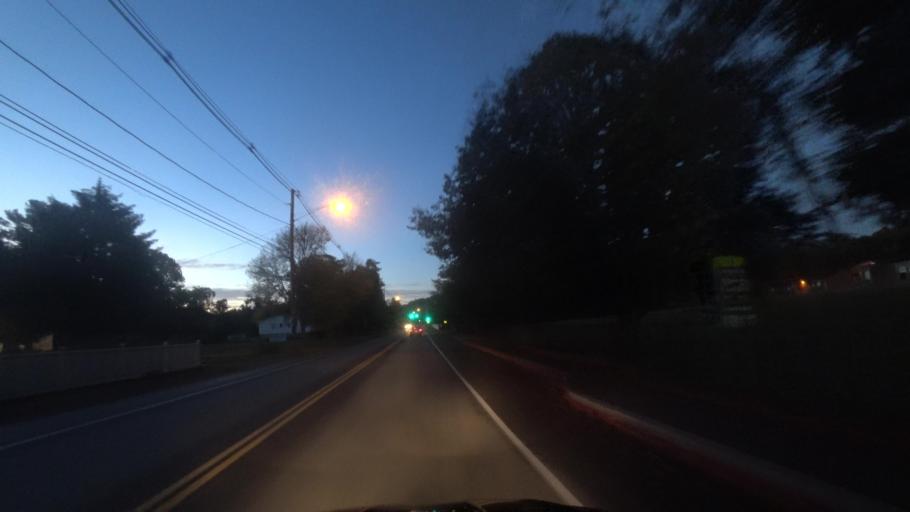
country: US
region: Massachusetts
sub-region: Middlesex County
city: Reading
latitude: 42.5421
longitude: -71.0888
